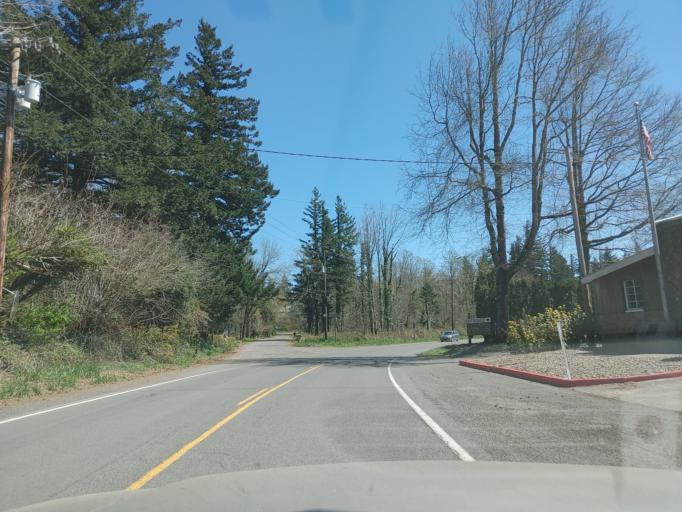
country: US
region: Washington
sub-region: Clark County
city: Washougal
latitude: 45.5320
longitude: -122.2837
